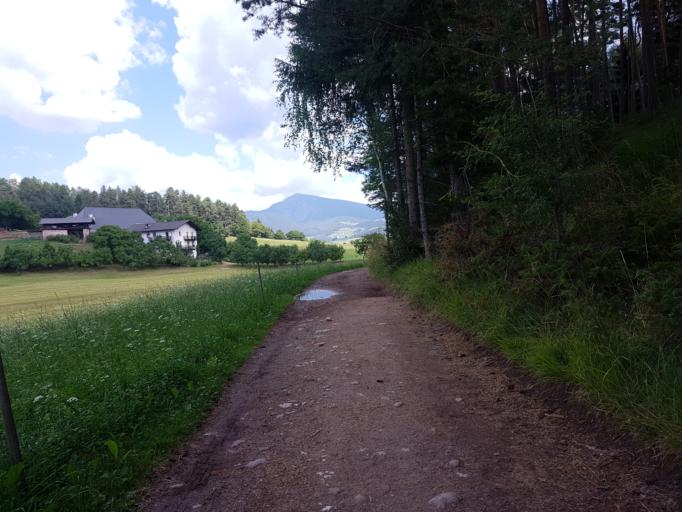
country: IT
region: Trentino-Alto Adige
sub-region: Bolzano
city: Castelrotto
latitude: 46.5600
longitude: 11.5449
